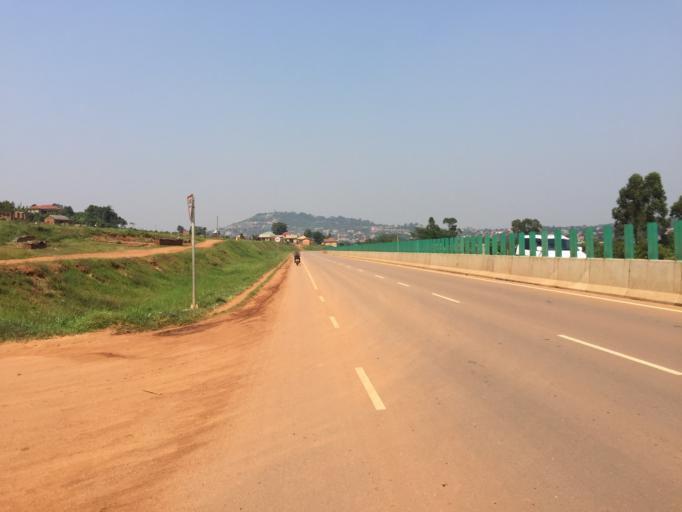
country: UG
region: Central Region
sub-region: Kampala District
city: Kampala
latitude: 0.2321
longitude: 32.6074
